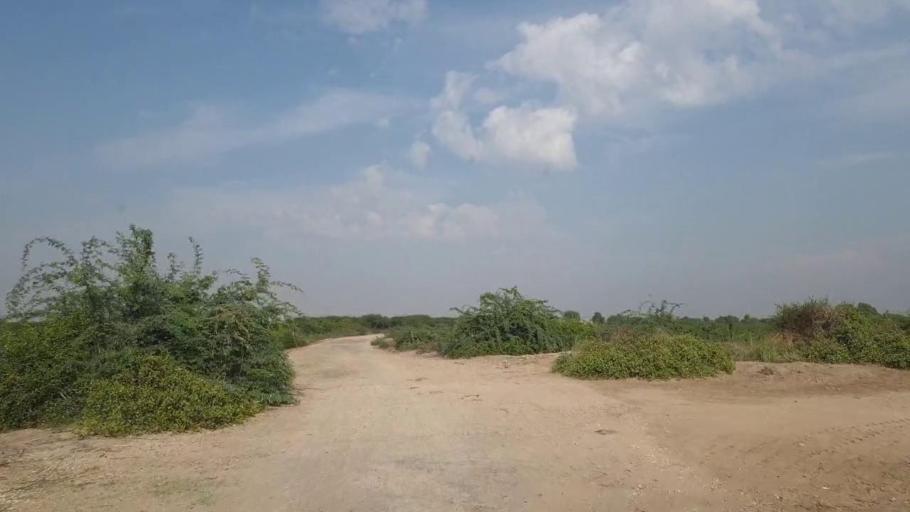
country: PK
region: Sindh
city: Digri
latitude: 25.0012
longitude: 69.0628
